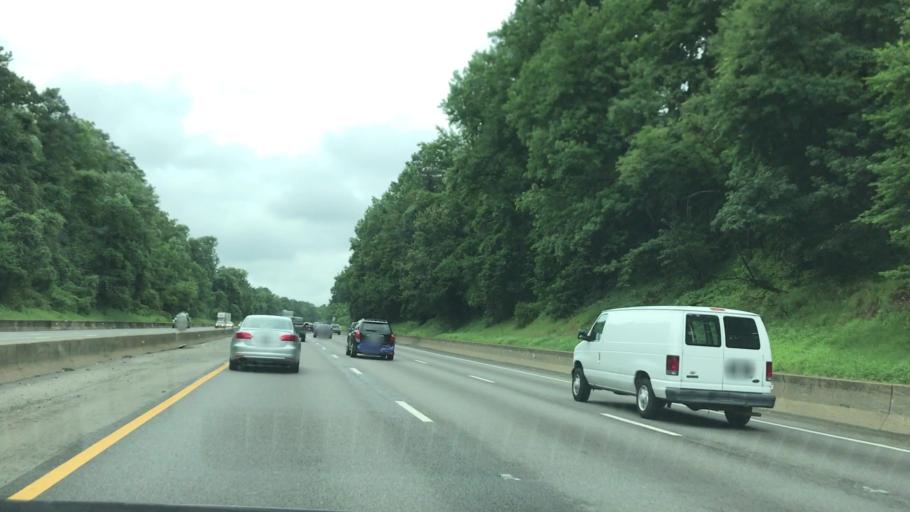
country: US
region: Virginia
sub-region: Chesterfield County
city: Chester
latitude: 37.3819
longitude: -77.4135
